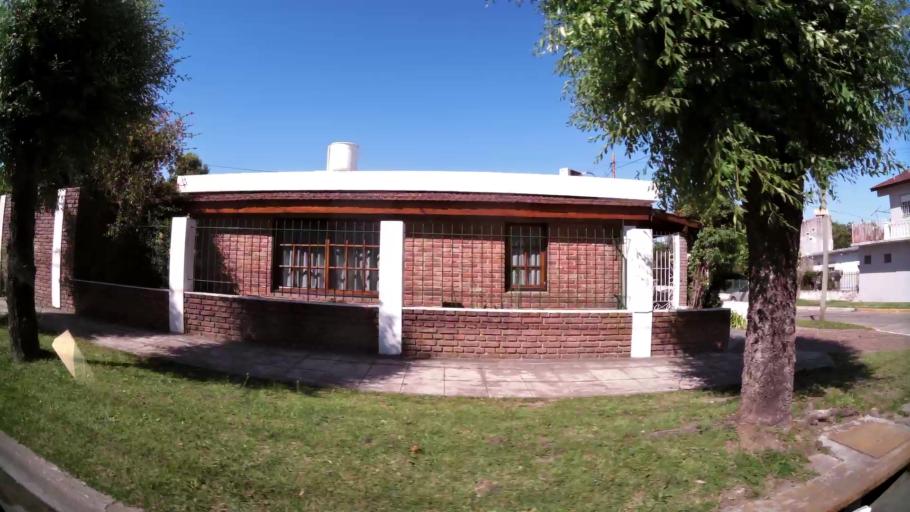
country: AR
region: Buenos Aires
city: Hurlingham
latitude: -34.4976
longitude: -58.6895
